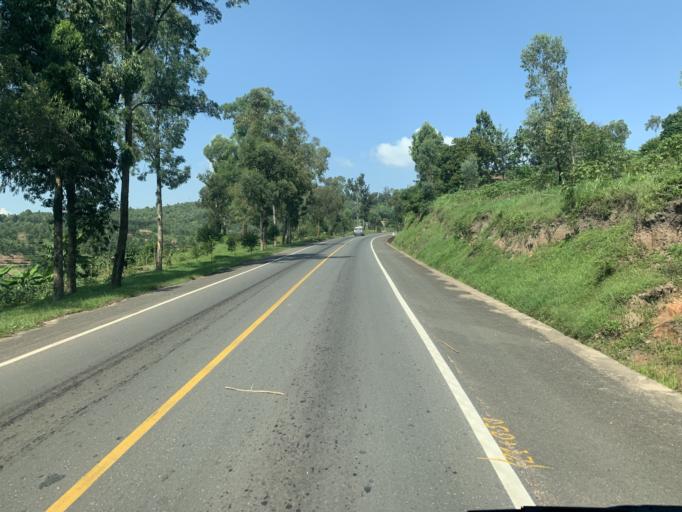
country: RW
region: Kigali
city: Kigali
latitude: -1.9931
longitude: 29.9231
